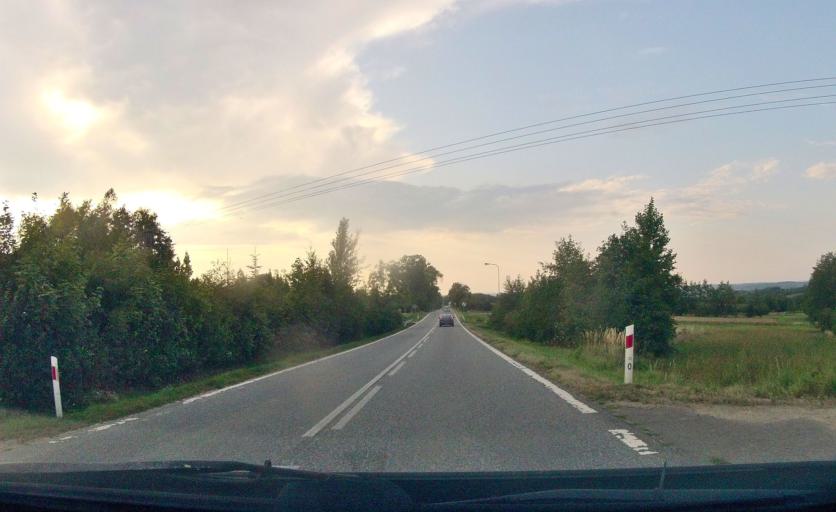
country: PL
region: Subcarpathian Voivodeship
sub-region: Powiat jasielski
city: Nowy Zmigrod
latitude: 49.5764
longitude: 21.5602
